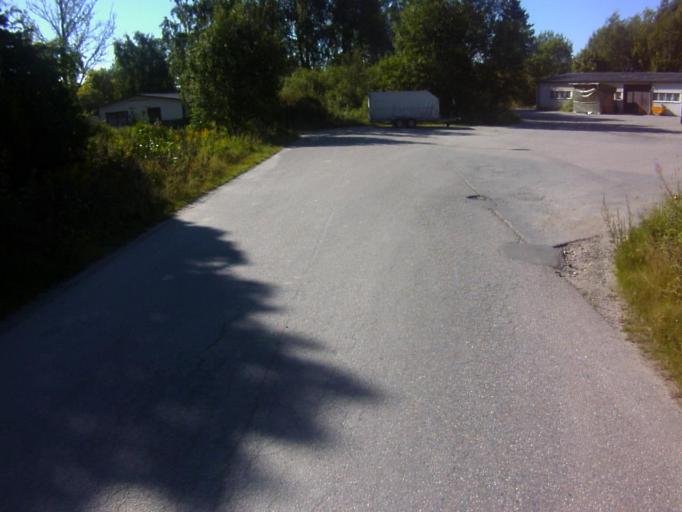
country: SE
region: Soedermanland
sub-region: Eskilstuna Kommun
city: Torshalla
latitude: 59.3860
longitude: 16.4796
